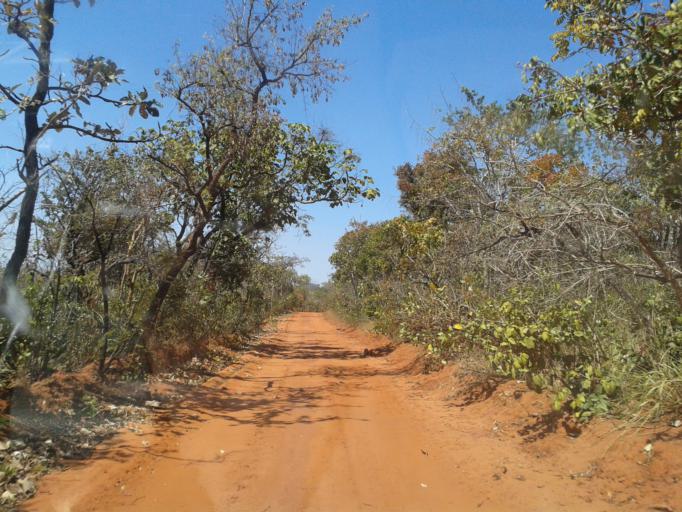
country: BR
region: Minas Gerais
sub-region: Monte Alegre De Minas
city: Monte Alegre de Minas
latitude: -18.8349
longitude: -49.0964
